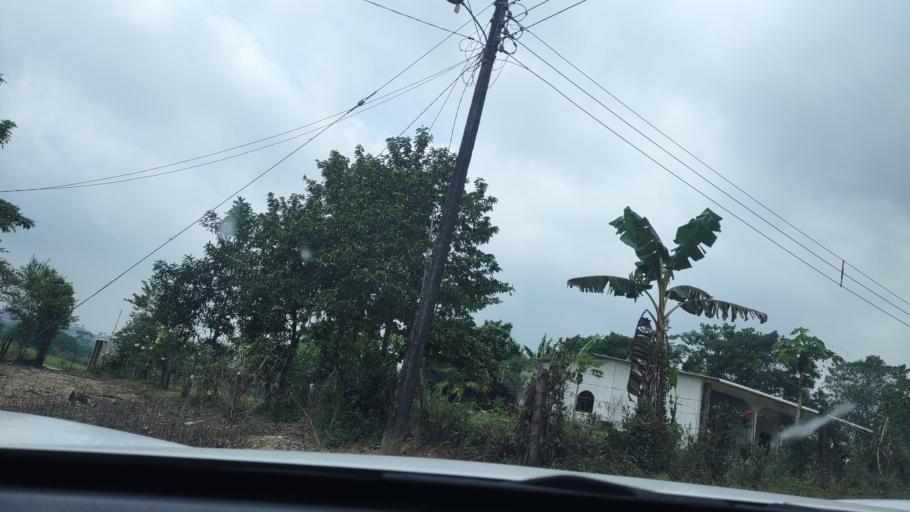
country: MX
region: Veracruz
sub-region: Uxpanapa
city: Poblado 10
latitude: 17.5211
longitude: -94.3044
